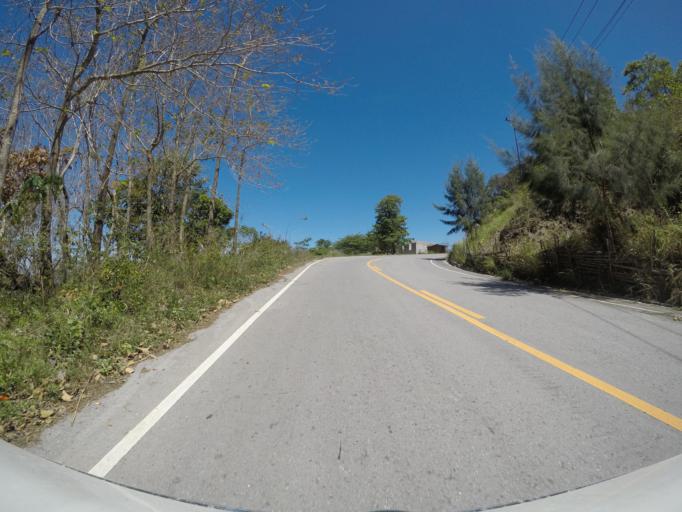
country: TL
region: Manatuto
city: Manatuto
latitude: -8.8066
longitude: 125.9713
